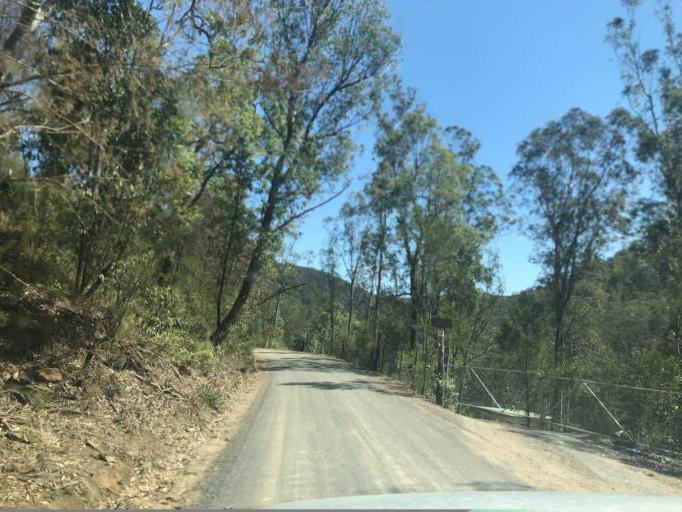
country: AU
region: New South Wales
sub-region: Wyong Shire
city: Little Jilliby
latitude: -33.1616
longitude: 151.0724
